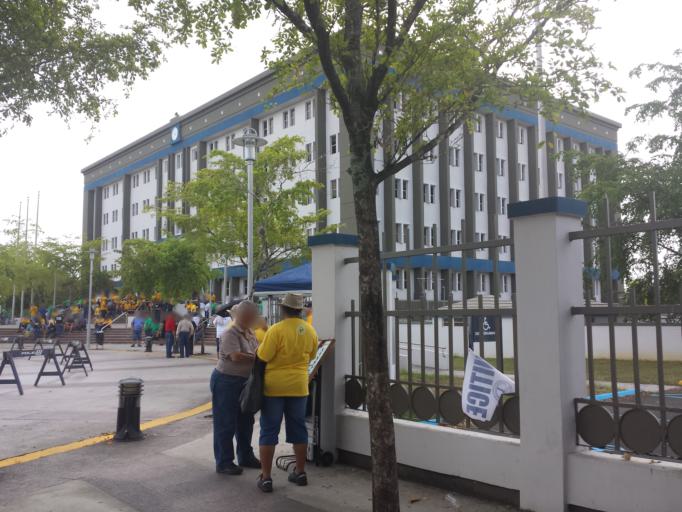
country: PR
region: Carolina
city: Carolina
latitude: 18.3832
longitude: -65.9549
